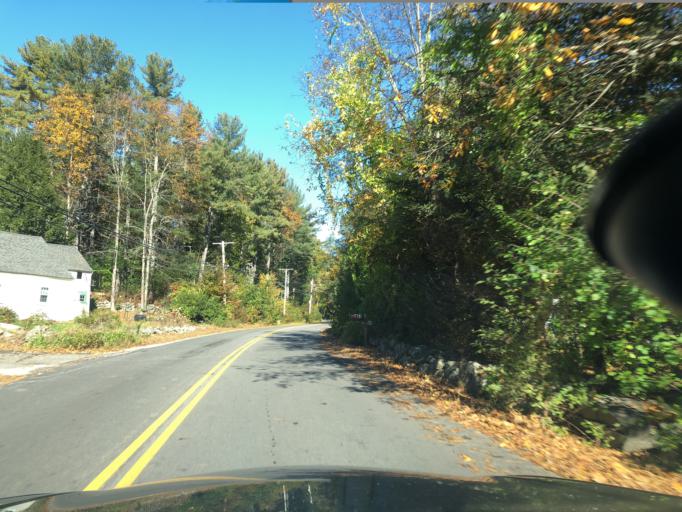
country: US
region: New Hampshire
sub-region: Rockingham County
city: Newmarket
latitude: 43.0892
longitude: -70.9473
